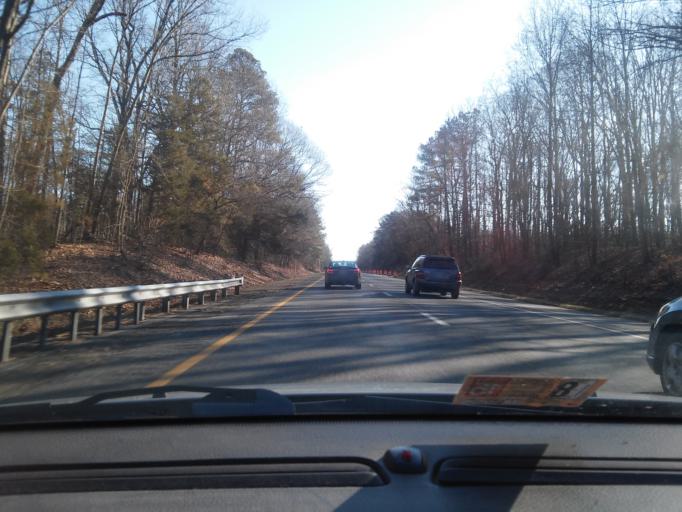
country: US
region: Virginia
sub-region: Henrico County
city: Wyndham
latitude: 37.6894
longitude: -77.6902
